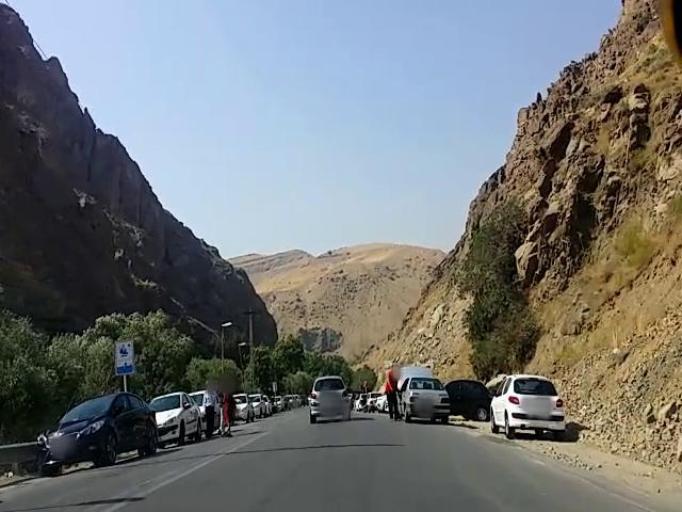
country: IR
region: Alborz
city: Karaj
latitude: 35.9074
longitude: 51.0432
